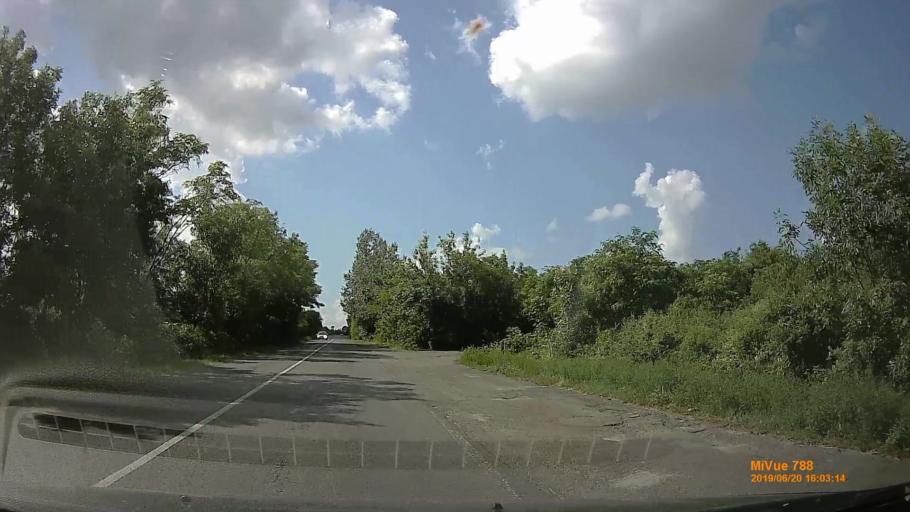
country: HU
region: Baranya
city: Pellerd
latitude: 46.0621
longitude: 18.1170
